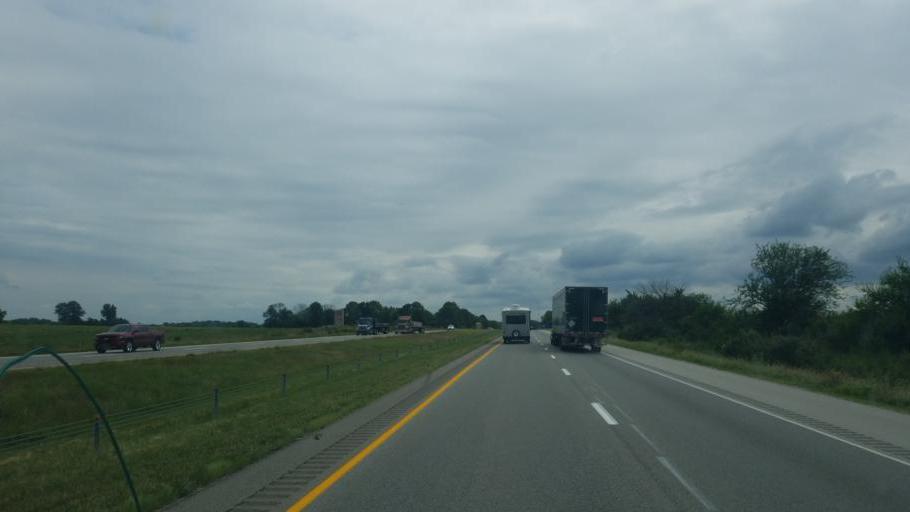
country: US
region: Indiana
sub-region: Morgan County
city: Monrovia
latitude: 39.6023
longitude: -86.5128
